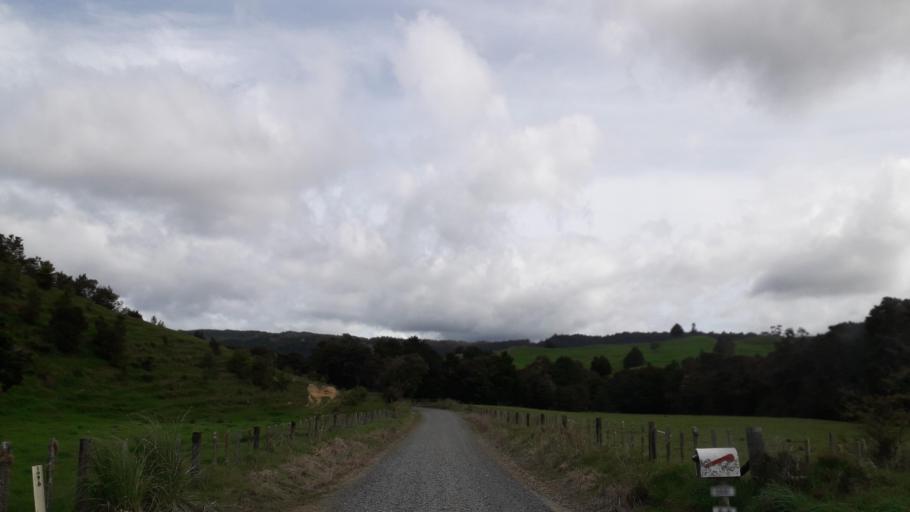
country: NZ
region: Northland
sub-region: Far North District
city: Waimate North
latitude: -35.1497
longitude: 173.7123
